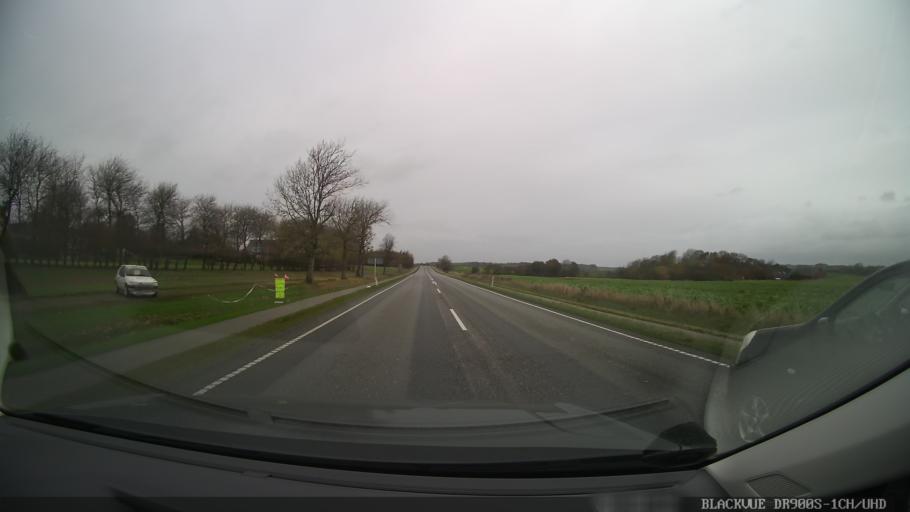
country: DK
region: North Denmark
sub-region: Thisted Kommune
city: Thisted
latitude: 56.8468
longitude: 8.7018
